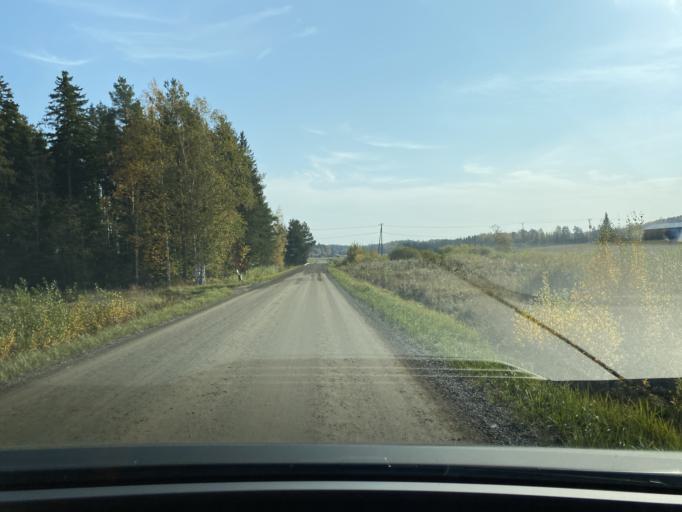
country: FI
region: Pirkanmaa
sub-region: Lounais-Pirkanmaa
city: Punkalaidun
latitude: 61.1324
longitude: 23.2344
